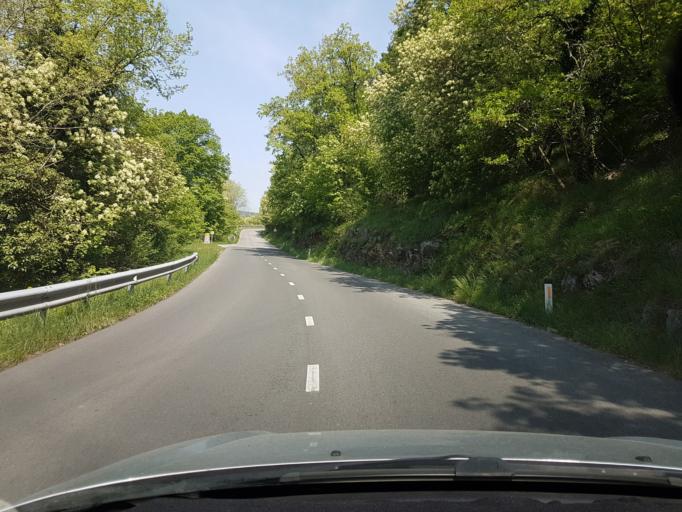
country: SI
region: Komen
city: Komen
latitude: 45.7980
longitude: 13.7108
